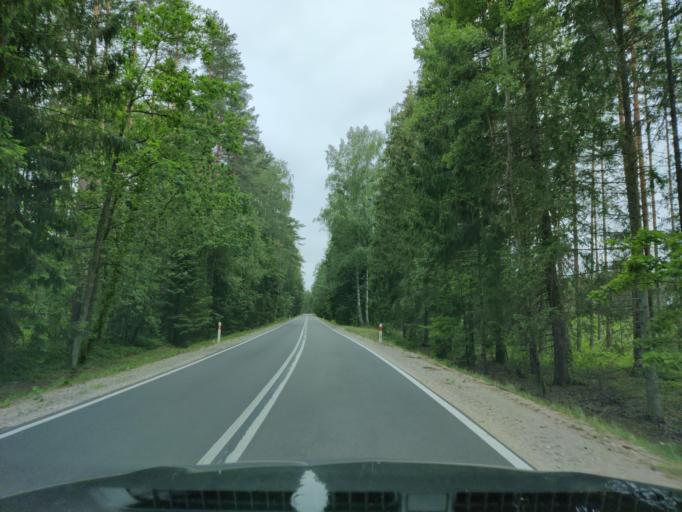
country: PL
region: Masovian Voivodeship
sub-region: Powiat ostrolecki
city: Czarnia
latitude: 53.3308
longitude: 21.1913
